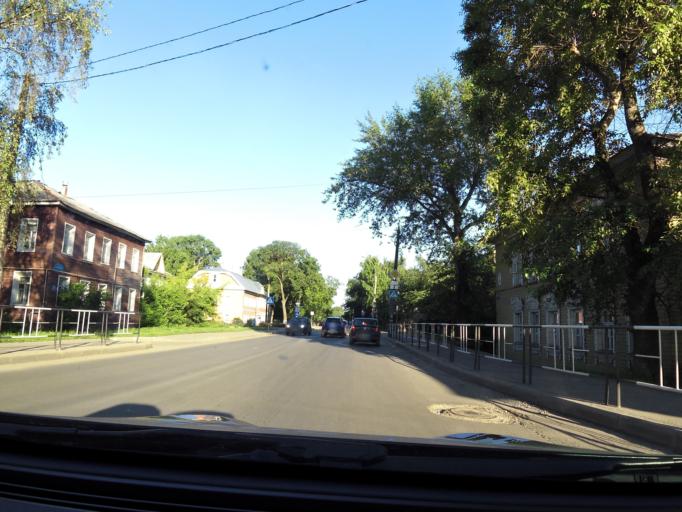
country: RU
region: Vologda
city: Vologda
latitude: 59.2094
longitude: 39.9084
